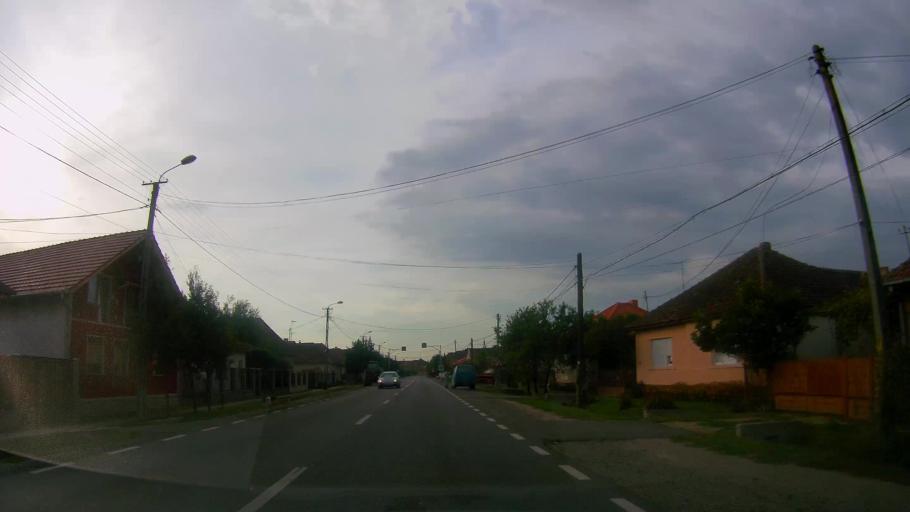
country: RO
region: Satu Mare
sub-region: Comuna Turulung
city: Turulung
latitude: 47.9418
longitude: 23.0784
